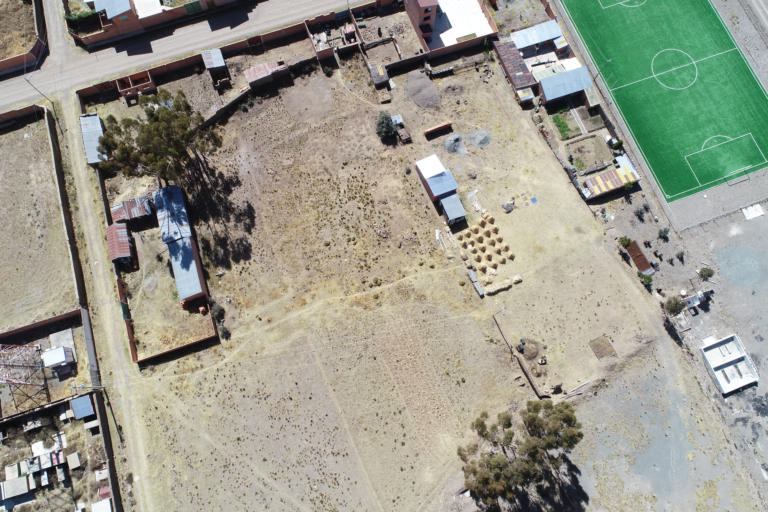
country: BO
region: La Paz
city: Achacachi
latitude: -15.9002
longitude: -68.9053
